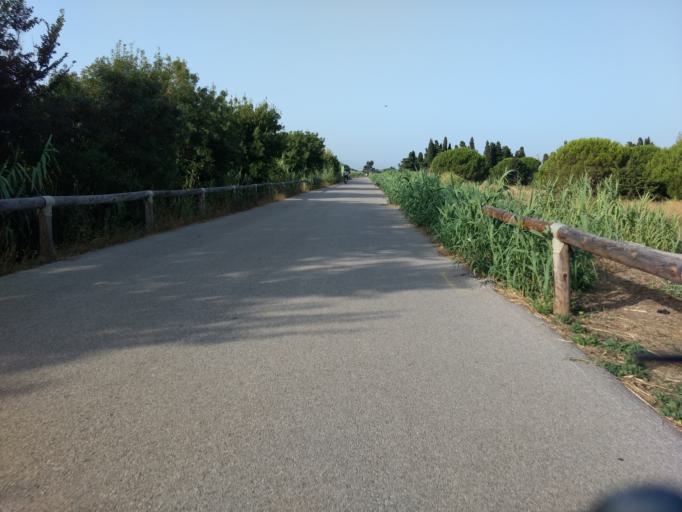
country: FR
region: Languedoc-Roussillon
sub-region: Departement des Pyrenees-Orientales
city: Le Barcares
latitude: 42.7744
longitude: 3.0281
